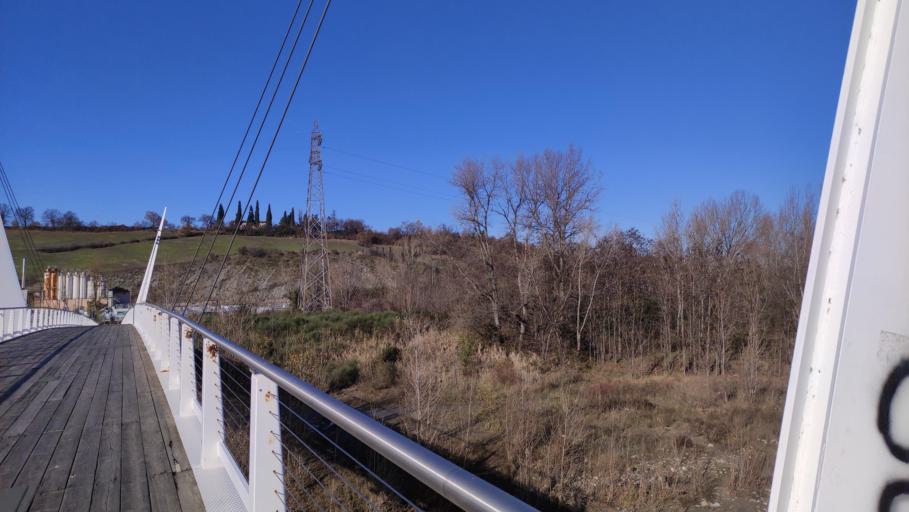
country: IT
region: Emilia-Romagna
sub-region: Provincia di Reggio Emilia
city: Veggia-Villalunga
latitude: 44.5431
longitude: 10.7674
